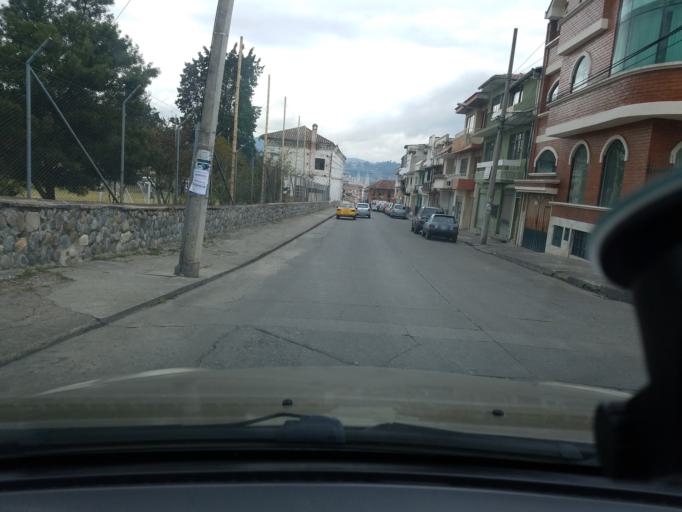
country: EC
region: Azuay
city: Cuenca
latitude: -2.8899
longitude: -79.0016
